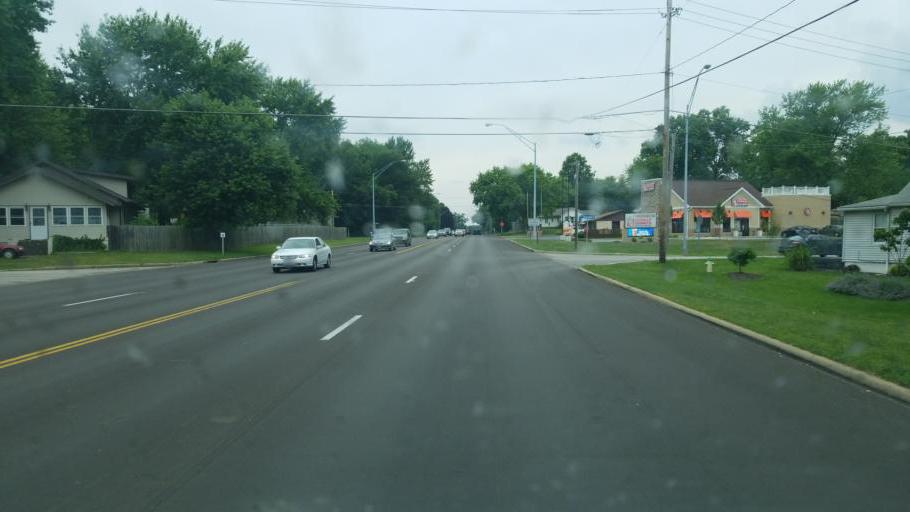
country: US
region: Ohio
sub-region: Summit County
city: Sawyerwood
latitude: 41.0321
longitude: -81.4315
